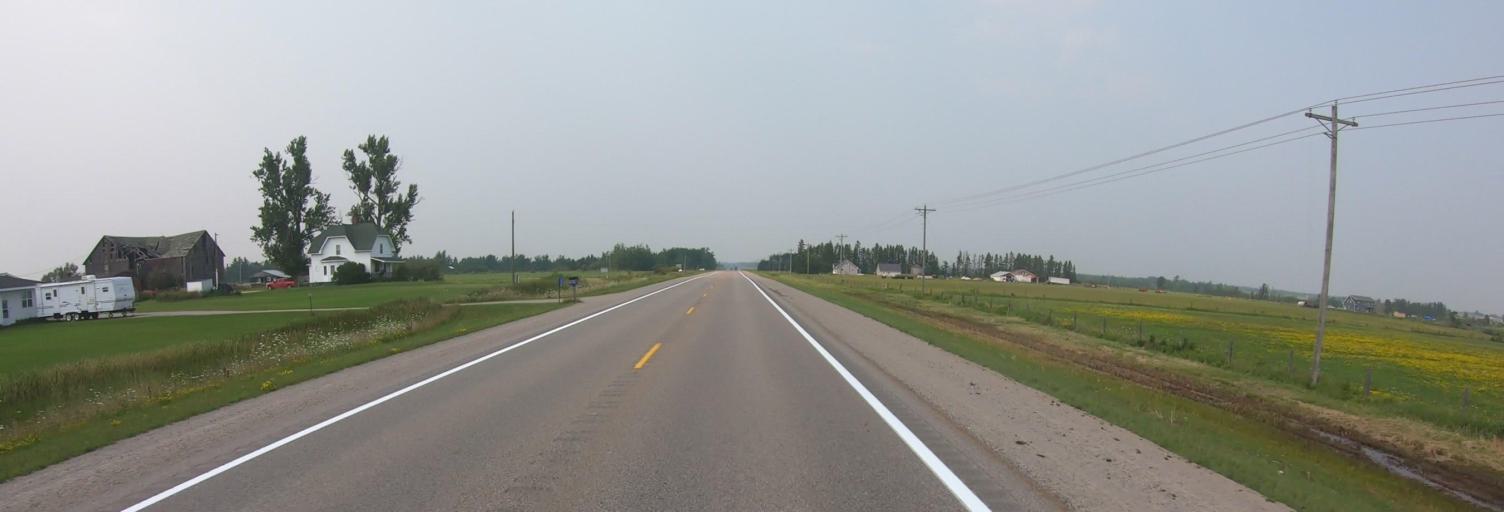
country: US
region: Michigan
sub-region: Chippewa County
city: Sault Ste. Marie
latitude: 46.3430
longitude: -84.3639
